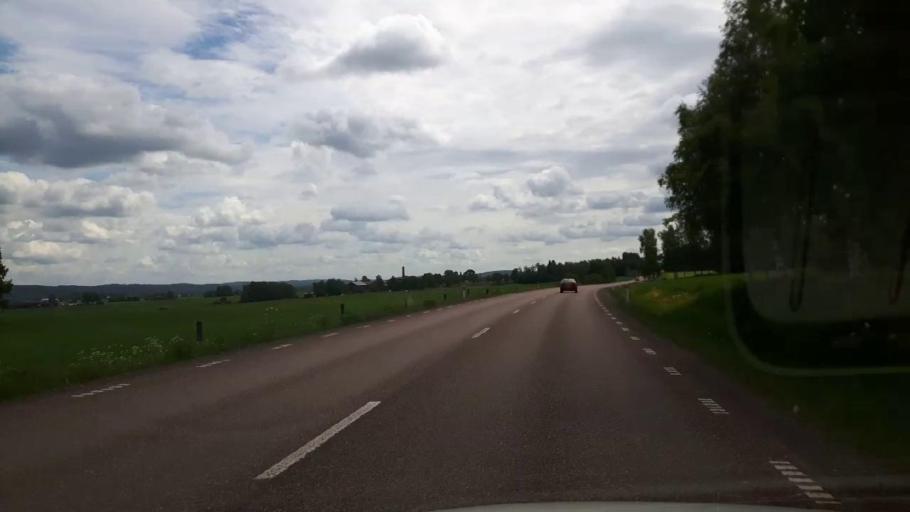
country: SE
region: Dalarna
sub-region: Hedemora Kommun
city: Hedemora
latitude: 60.3099
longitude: 15.9706
